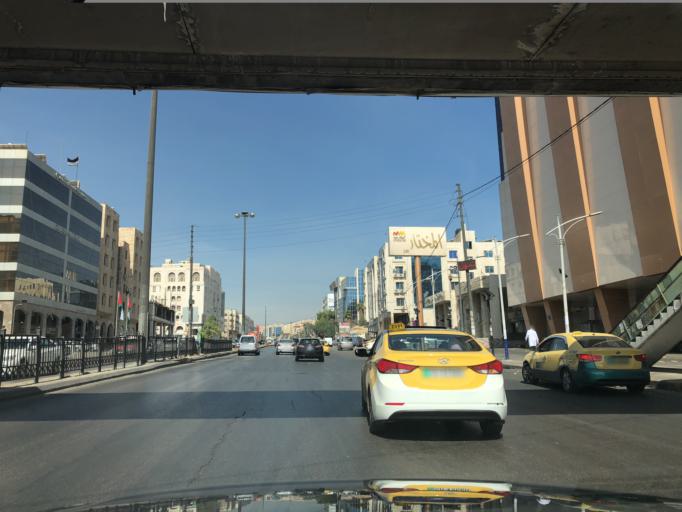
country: JO
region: Amman
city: Al Jubayhah
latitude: 31.9872
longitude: 35.8965
